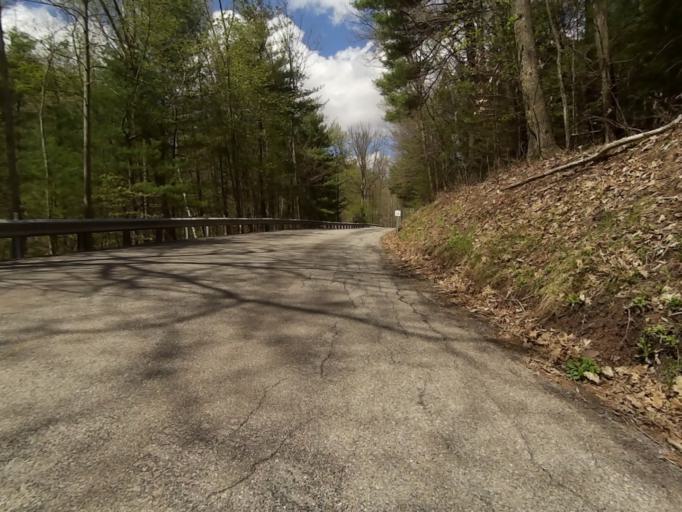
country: US
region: Pennsylvania
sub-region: Centre County
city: Milesburg
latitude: 40.9550
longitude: -77.8910
